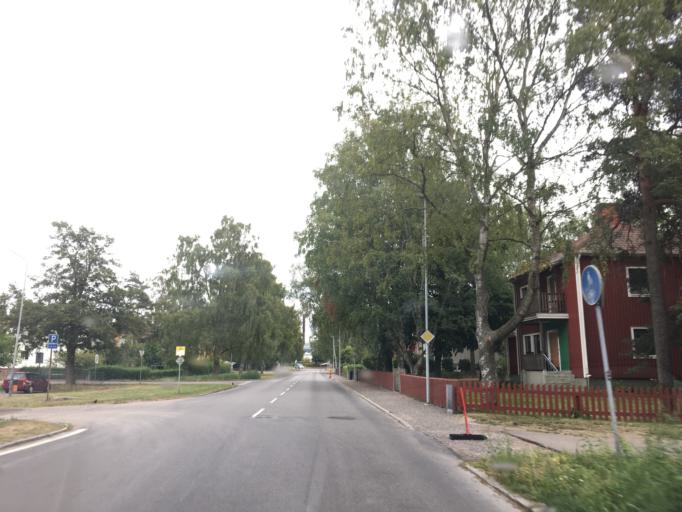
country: SE
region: Kalmar
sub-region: Nybro Kommun
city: Nybro
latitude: 56.7465
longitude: 15.9059
